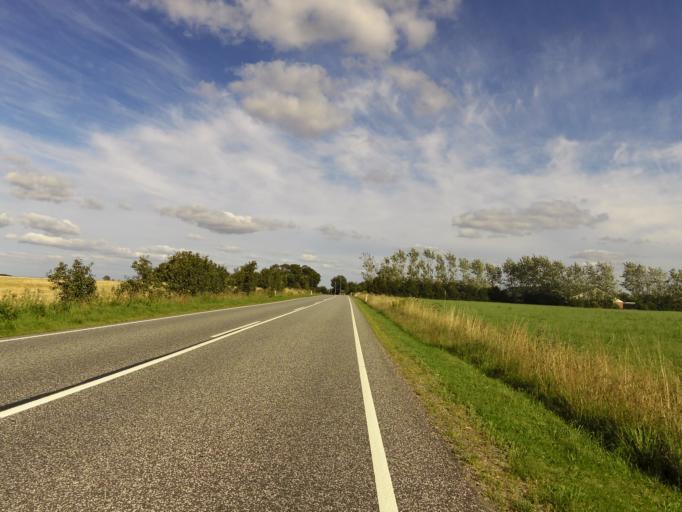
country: DK
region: South Denmark
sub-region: Haderslev Kommune
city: Gram
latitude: 55.2293
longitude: 8.9865
